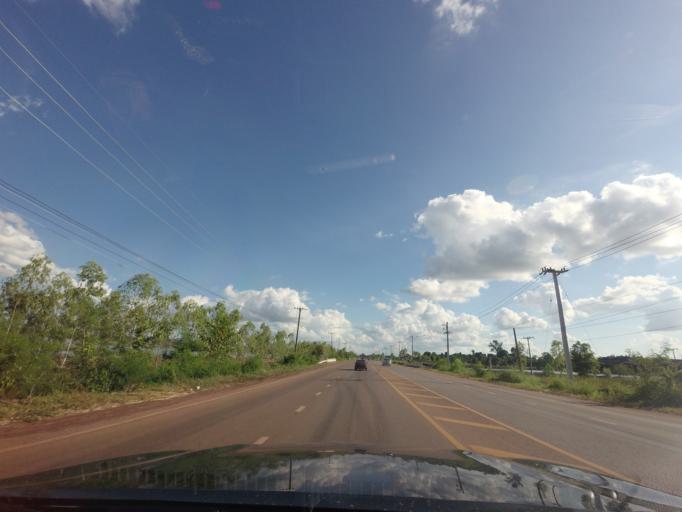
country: TH
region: Changwat Udon Thani
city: Ban Dung
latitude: 17.7202
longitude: 103.2502
